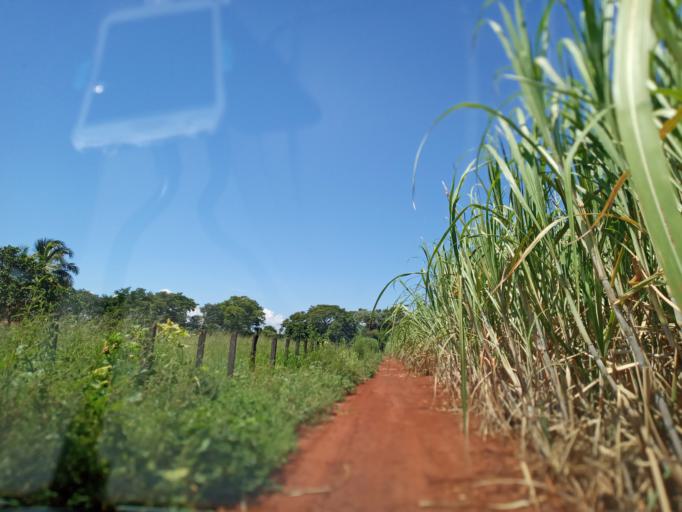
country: BR
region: Goias
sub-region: Itumbiara
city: Itumbiara
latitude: -18.4409
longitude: -49.1345
